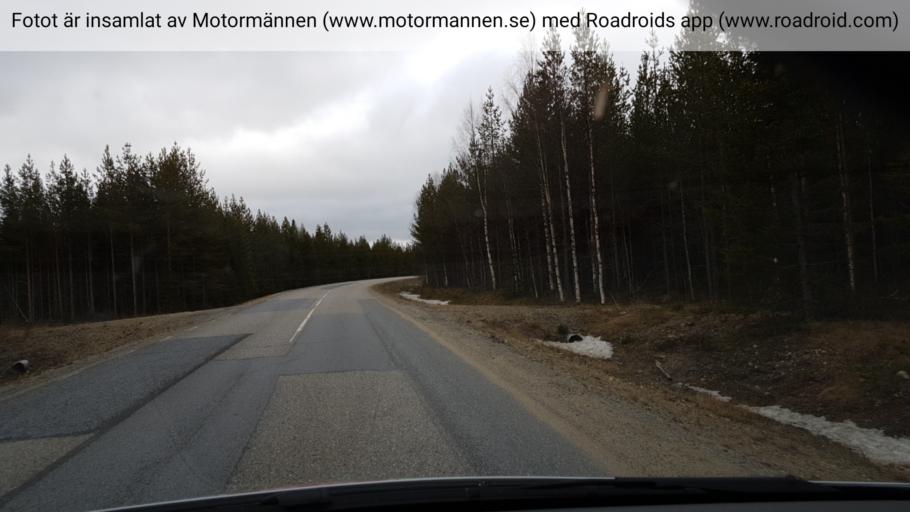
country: SE
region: Vaesterbotten
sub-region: Lycksele Kommun
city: Lycksele
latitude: 64.0566
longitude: 18.4152
